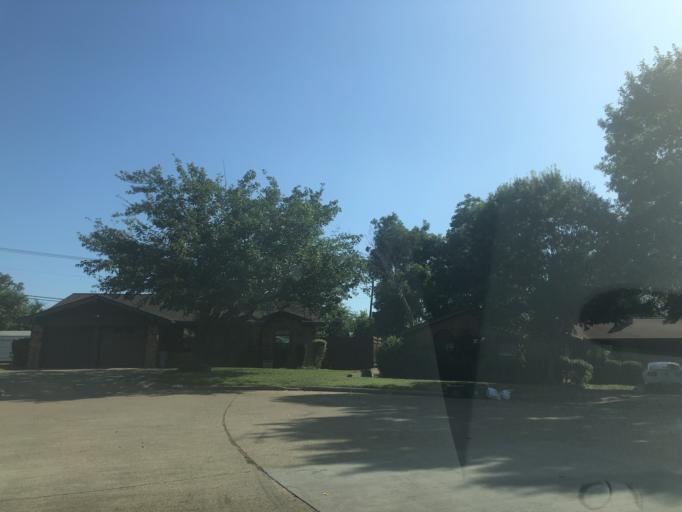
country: US
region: Texas
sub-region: Dallas County
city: Grand Prairie
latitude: 32.7587
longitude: -97.0250
